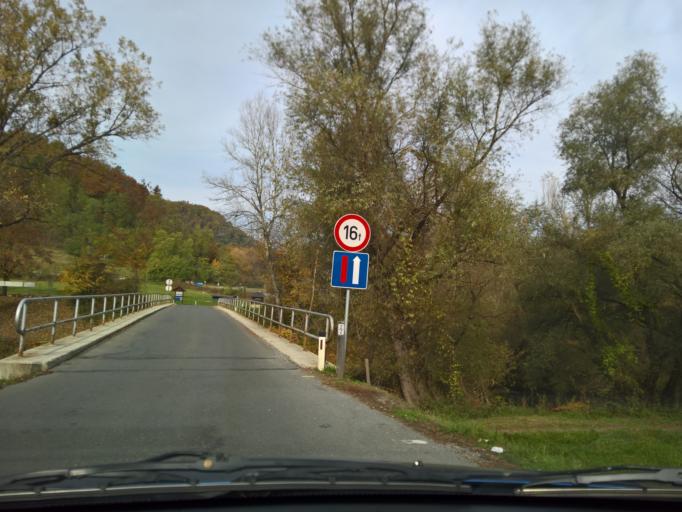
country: AT
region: Styria
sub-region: Politischer Bezirk Leibnitz
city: Seggauberg
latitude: 46.7771
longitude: 15.5196
